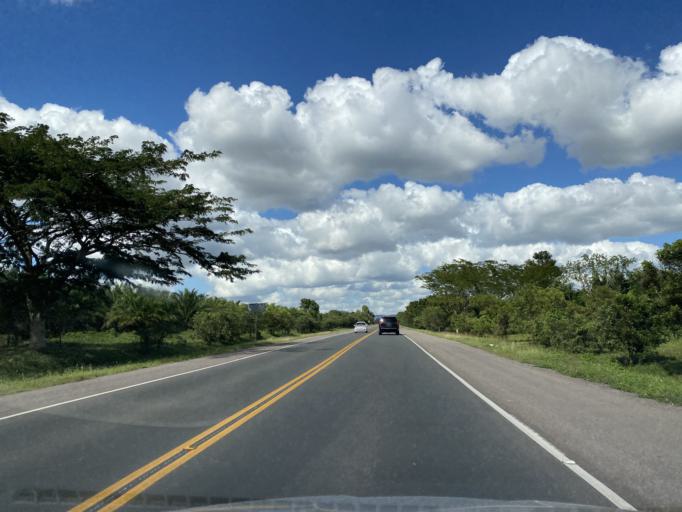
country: DO
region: Monte Plata
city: Monte Plata
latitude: 18.7307
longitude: -69.7612
